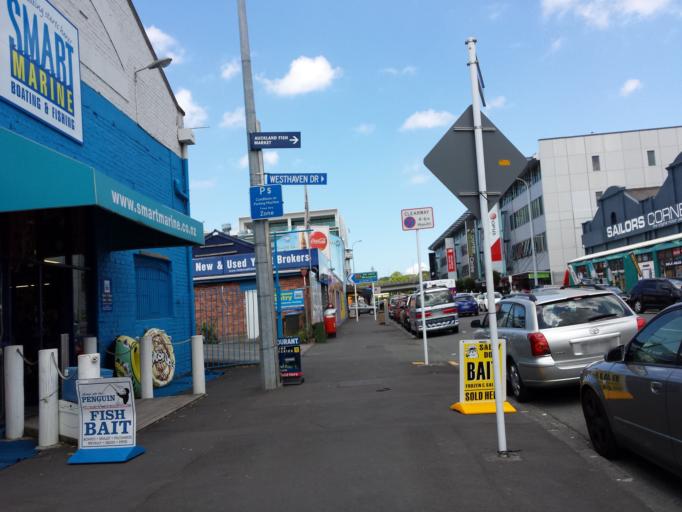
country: NZ
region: Auckland
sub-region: Auckland
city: Auckland
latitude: -36.8433
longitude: 174.7538
